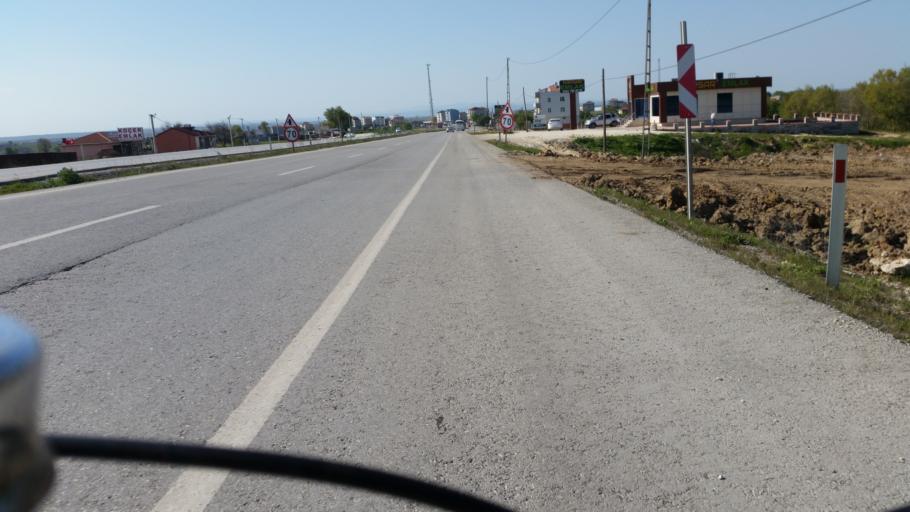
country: TR
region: Tekirdag
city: Cerkezkoey
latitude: 41.3497
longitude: 27.9585
